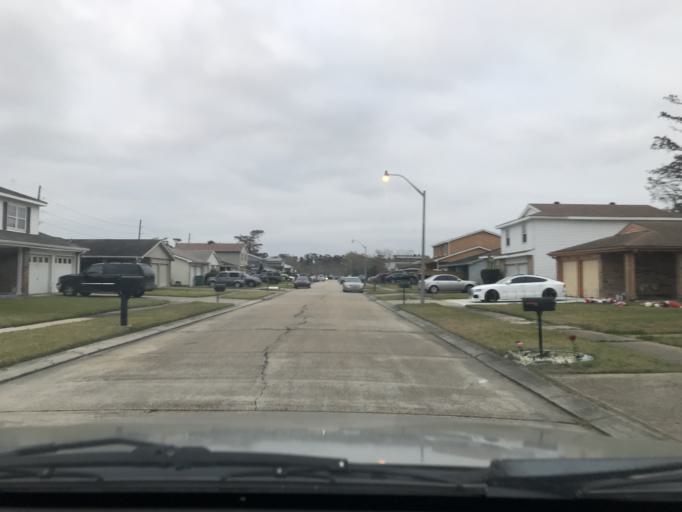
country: US
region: Louisiana
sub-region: Jefferson Parish
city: Woodmere
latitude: 29.8595
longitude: -90.0770
